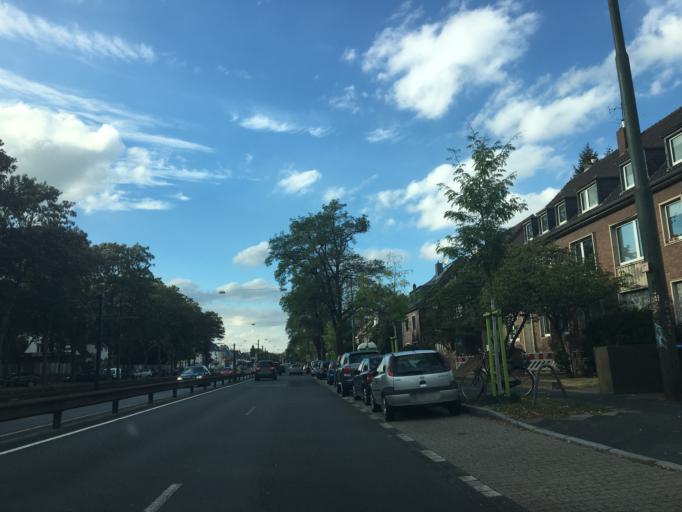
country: DE
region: North Rhine-Westphalia
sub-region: Regierungsbezirk Dusseldorf
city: Dusseldorf
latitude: 51.1987
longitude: 6.7930
